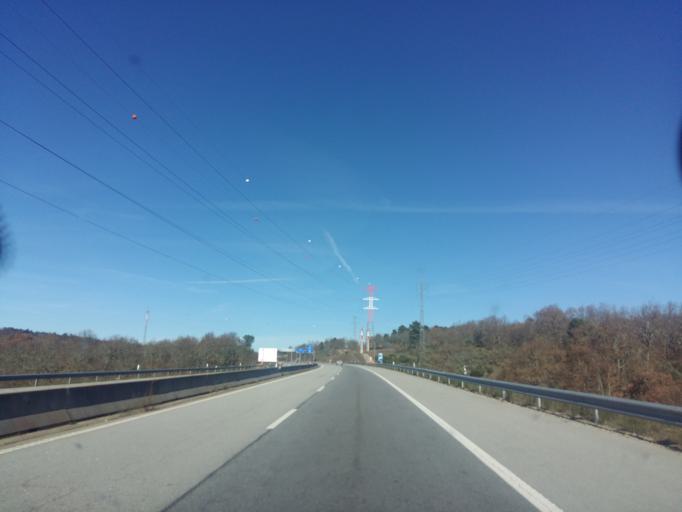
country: PT
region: Guarda
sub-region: Guarda
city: Sequeira
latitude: 40.5551
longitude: -7.2169
